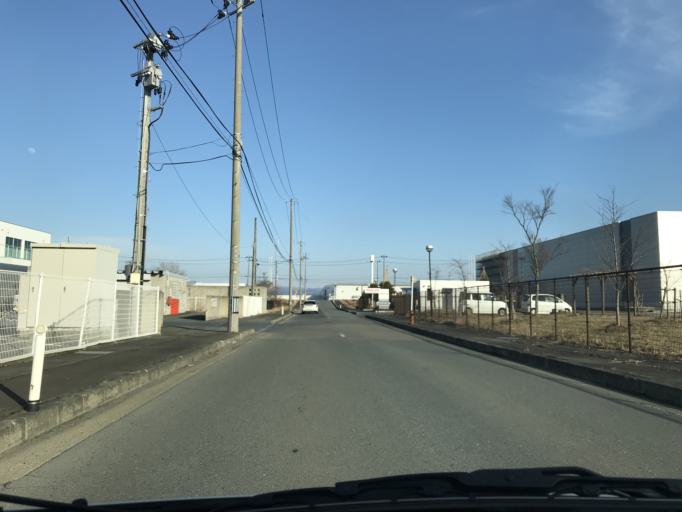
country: JP
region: Iwate
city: Kitakami
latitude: 39.2412
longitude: 141.0825
